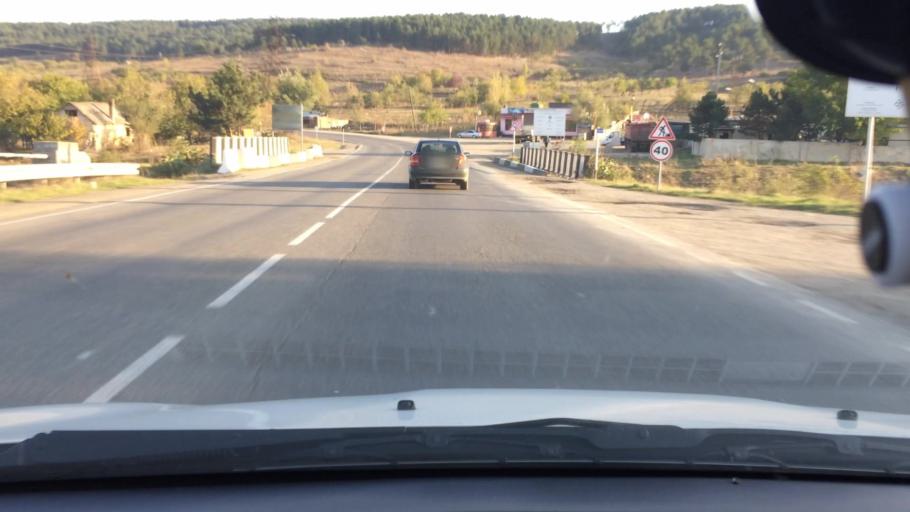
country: GE
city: Surami
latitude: 42.0100
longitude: 43.5777
